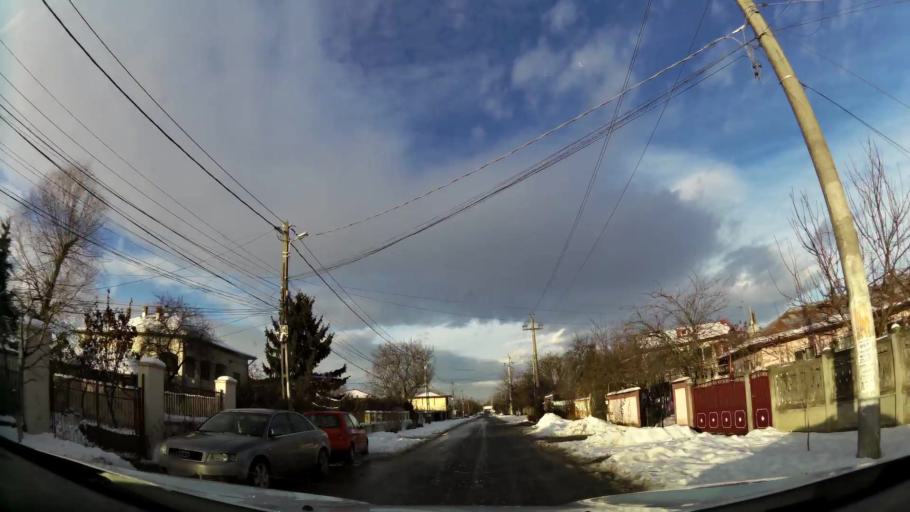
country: RO
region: Ilfov
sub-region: Comuna Jilava
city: Jilava
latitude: 44.3377
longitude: 26.0831
